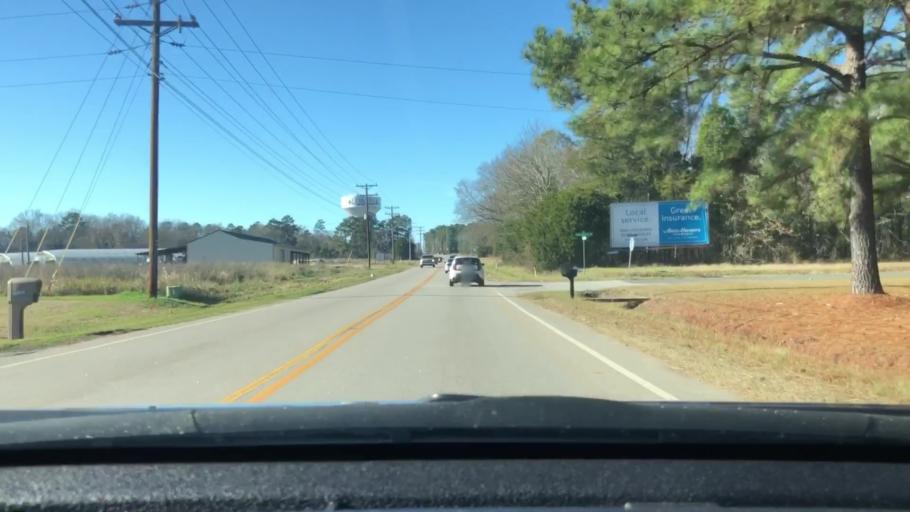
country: US
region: South Carolina
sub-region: Lexington County
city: Irmo
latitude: 34.1164
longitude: -81.2000
